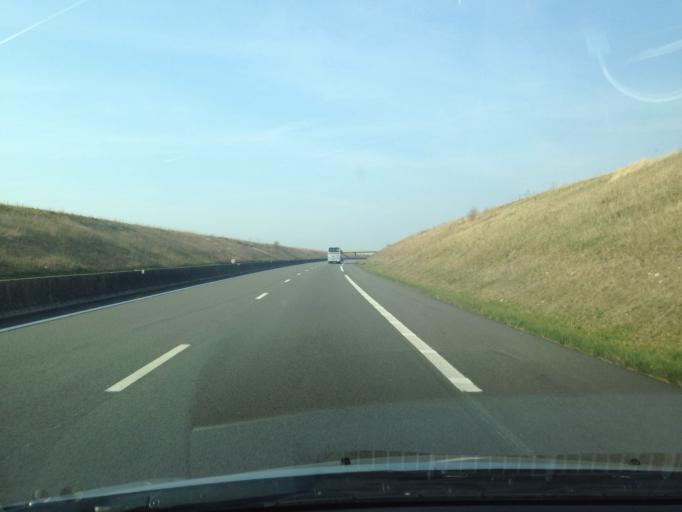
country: FR
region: Nord-Pas-de-Calais
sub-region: Departement du Pas-de-Calais
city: Verton
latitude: 50.3541
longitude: 1.6887
